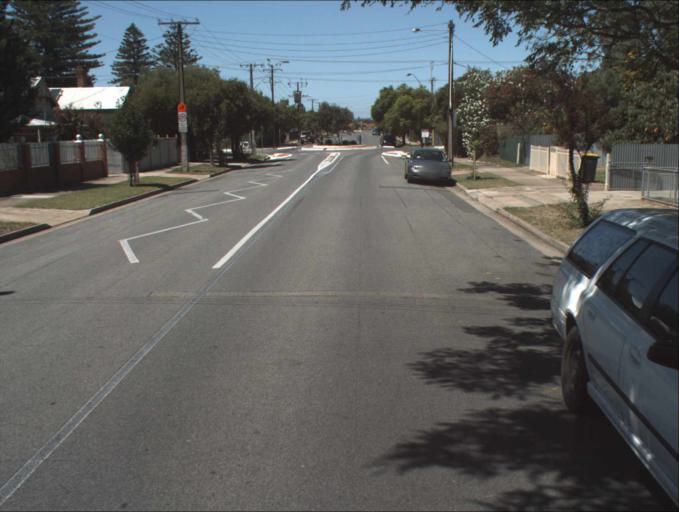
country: AU
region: South Australia
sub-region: Port Adelaide Enfield
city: Cheltenham
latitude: -34.8621
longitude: 138.5106
